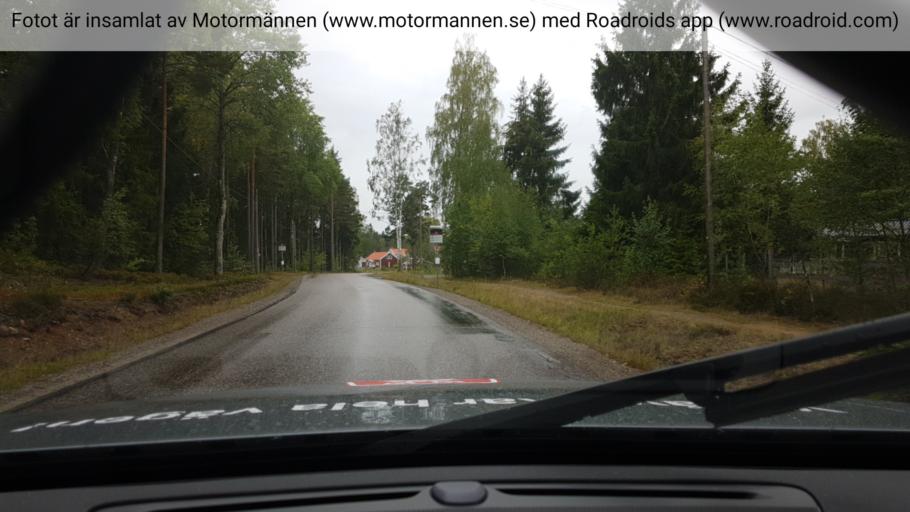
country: SE
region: Stockholm
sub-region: Nynashamns Kommun
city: Osmo
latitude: 59.0607
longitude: 17.8728
